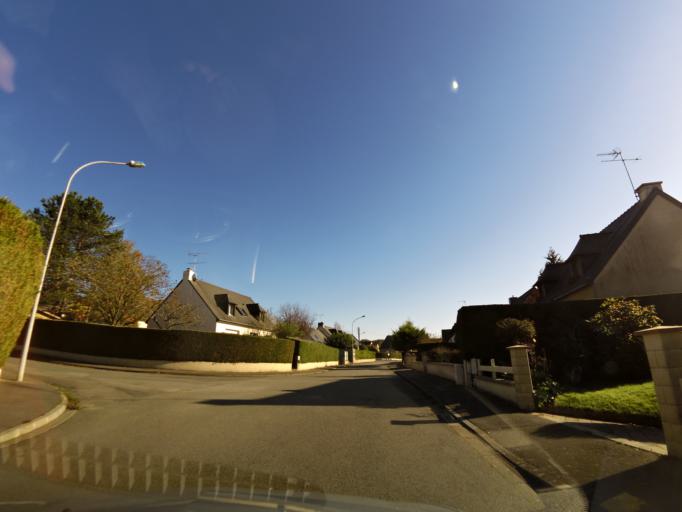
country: FR
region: Brittany
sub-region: Departement d'Ille-et-Vilaine
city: Bain-de-Bretagne
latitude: 47.8382
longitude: -1.6899
